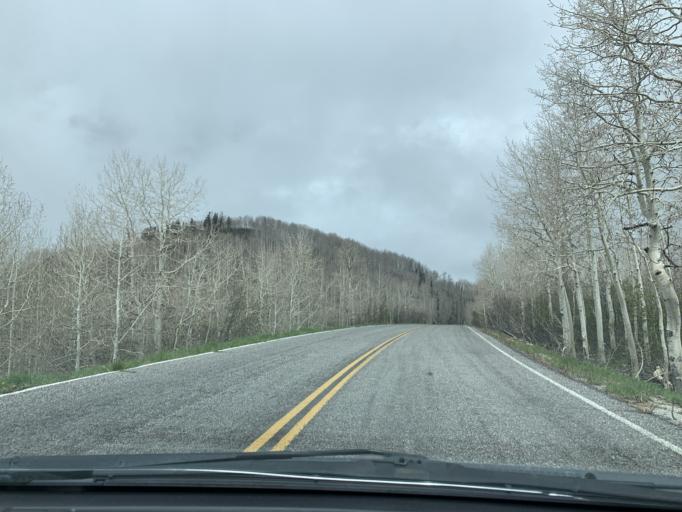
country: US
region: Utah
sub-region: Utah County
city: Elk Ridge
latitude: 39.8778
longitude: -111.6841
